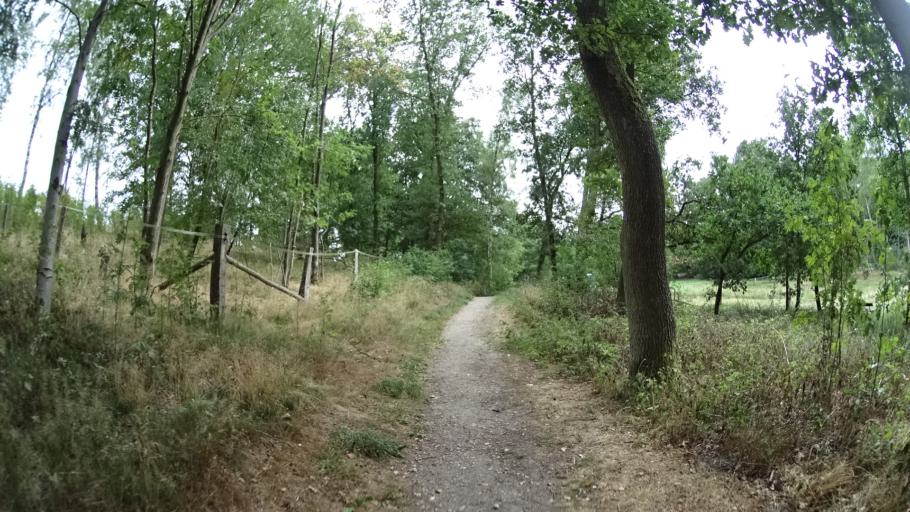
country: DE
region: Lower Saxony
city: Undeloh
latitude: 53.1930
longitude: 9.9790
